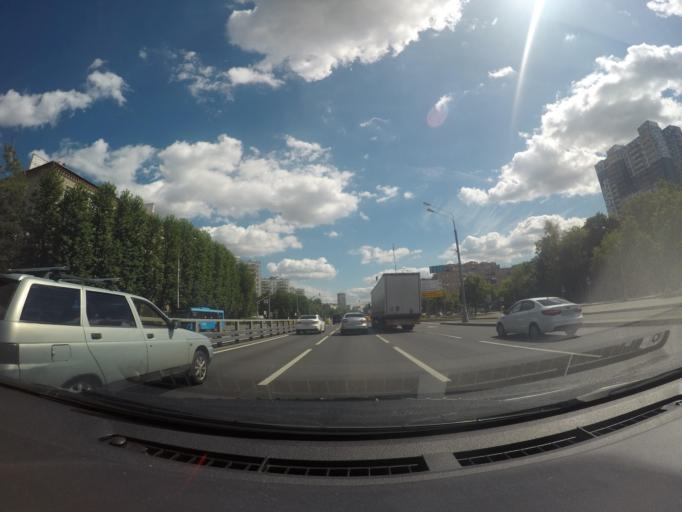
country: RU
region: Moscow
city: Novokuz'minki
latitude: 55.7170
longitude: 37.7951
